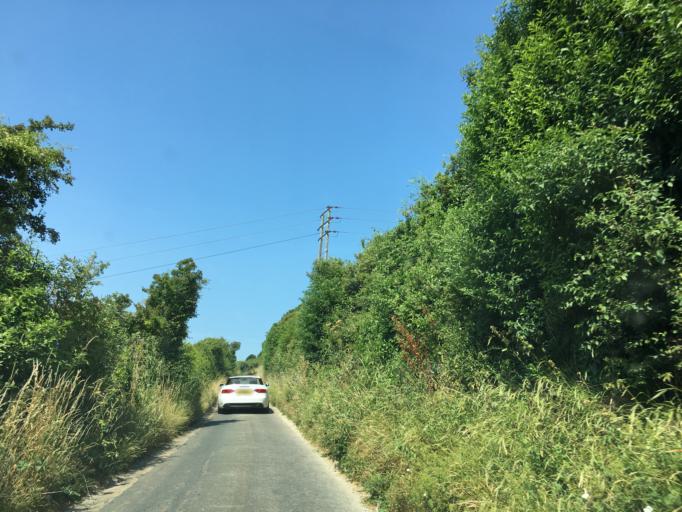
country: GB
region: England
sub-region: Isle of Wight
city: Newchurch
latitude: 50.6809
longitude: -1.2207
